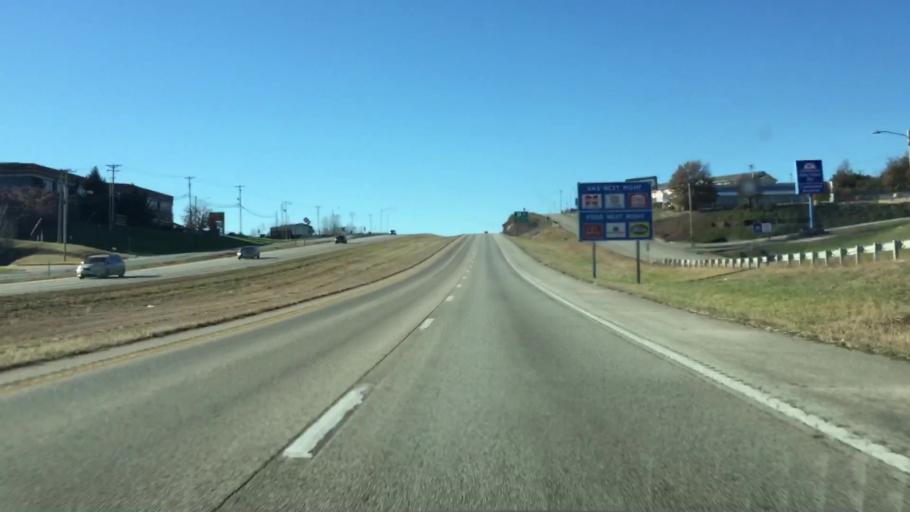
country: US
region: Missouri
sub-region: Cole County
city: Jefferson City
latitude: 38.5587
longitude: -92.1918
